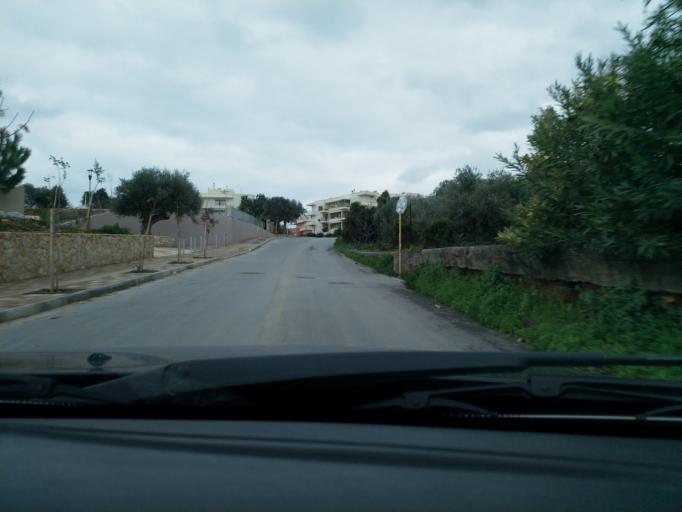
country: GR
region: Crete
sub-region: Nomos Chanias
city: Chania
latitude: 35.5116
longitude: 24.0377
